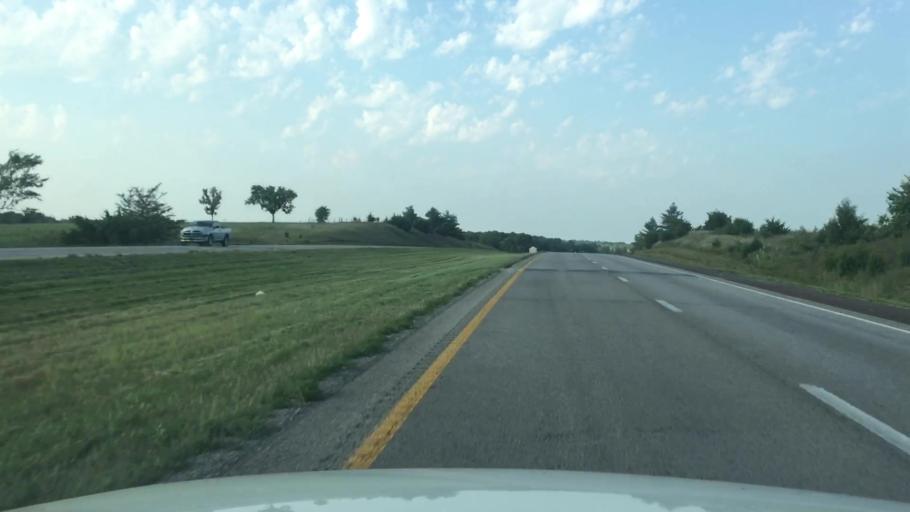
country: US
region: Missouri
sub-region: Clinton County
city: Cameron
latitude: 39.8692
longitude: -94.1696
